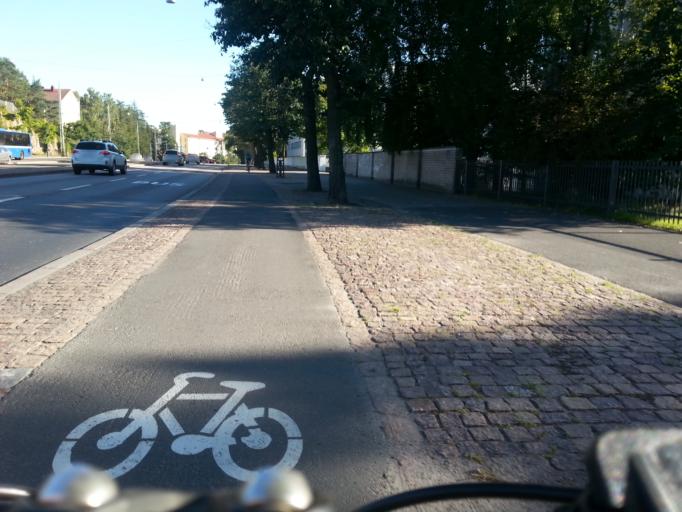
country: FI
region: Uusimaa
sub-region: Helsinki
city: Helsinki
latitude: 60.2007
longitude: 24.8992
